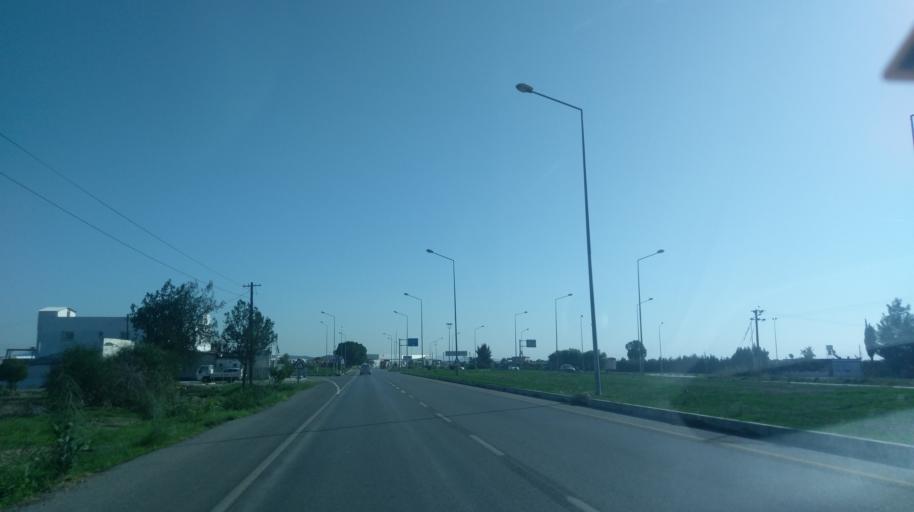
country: CY
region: Ammochostos
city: Lefkonoiko
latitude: 35.2081
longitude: 33.5902
